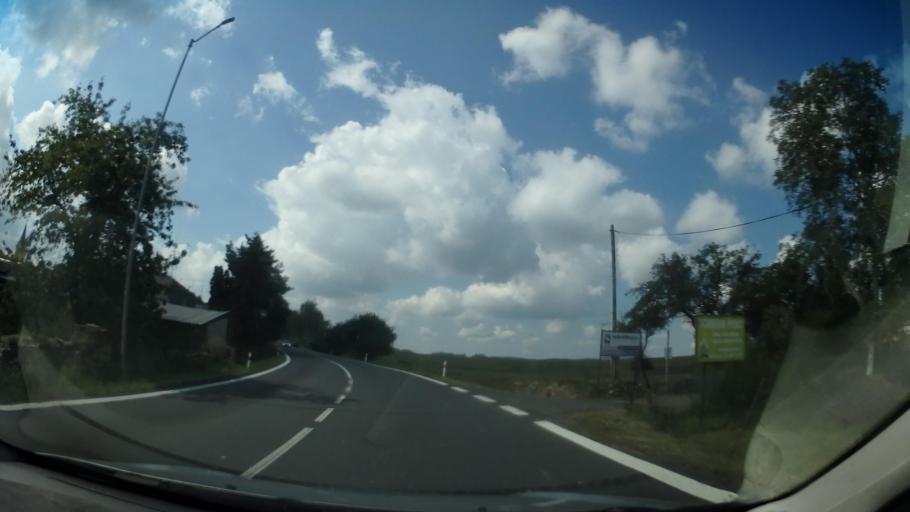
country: CZ
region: Central Bohemia
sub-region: Okres Kolin
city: Kourim
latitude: 49.9665
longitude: 14.9795
